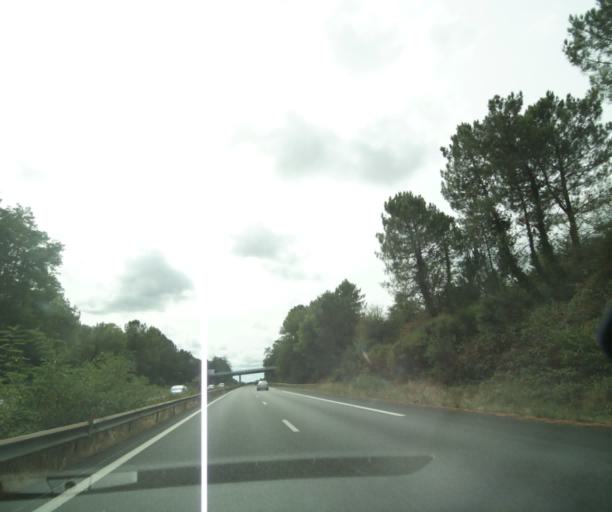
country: FR
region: Aquitaine
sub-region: Departement de la Gironde
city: Reignac
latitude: 45.2179
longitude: -0.5078
